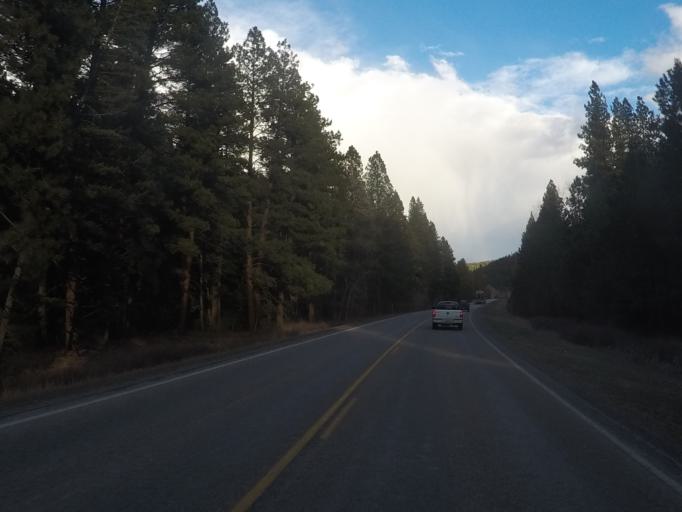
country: US
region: Montana
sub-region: Missoula County
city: Lolo
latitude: 46.7468
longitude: -114.1683
